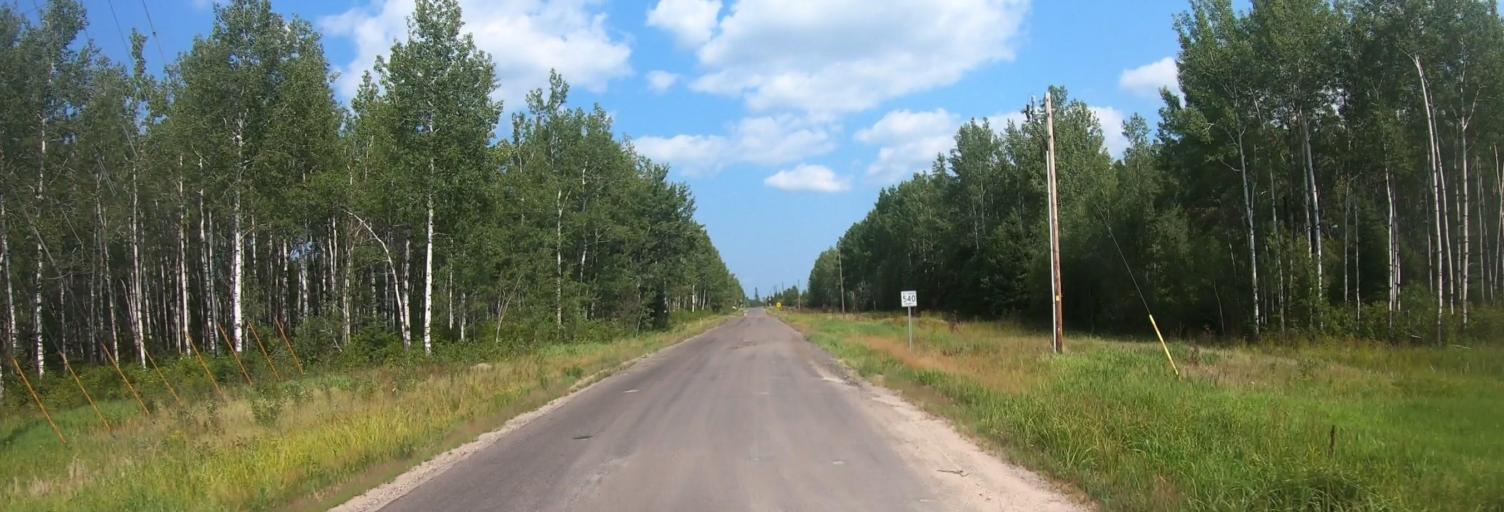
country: US
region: Minnesota
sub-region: Saint Louis County
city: Mountain Iron
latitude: 47.8920
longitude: -92.7183
